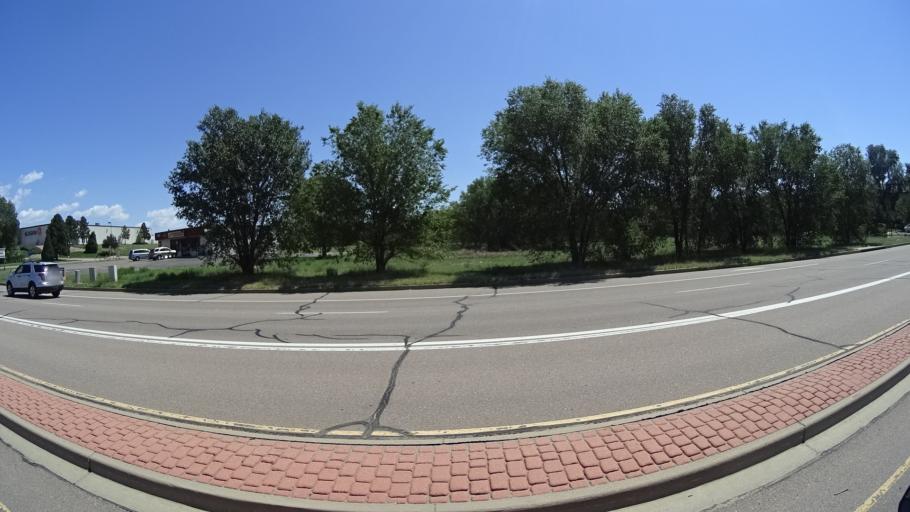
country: US
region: Colorado
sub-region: El Paso County
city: Security-Widefield
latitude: 38.7748
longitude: -104.7388
